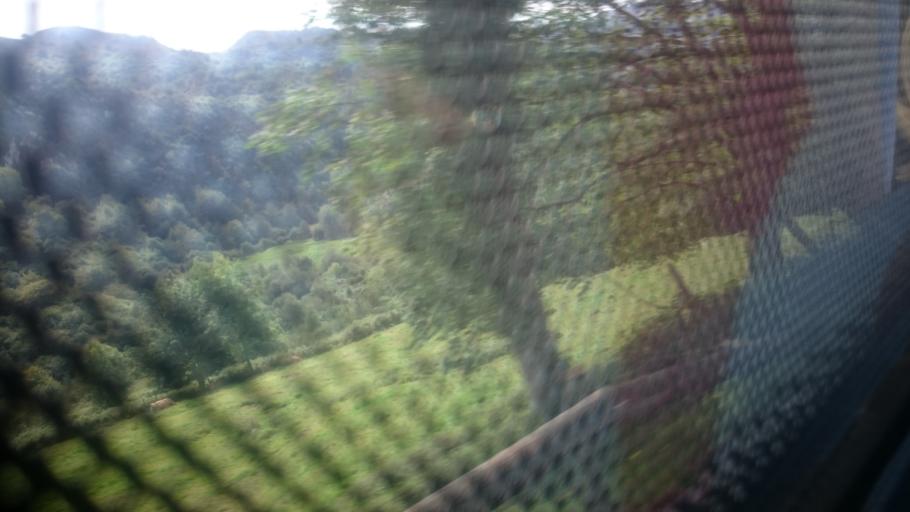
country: ES
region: Asturias
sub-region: Province of Asturias
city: Amieva
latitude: 43.2968
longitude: -5.0232
